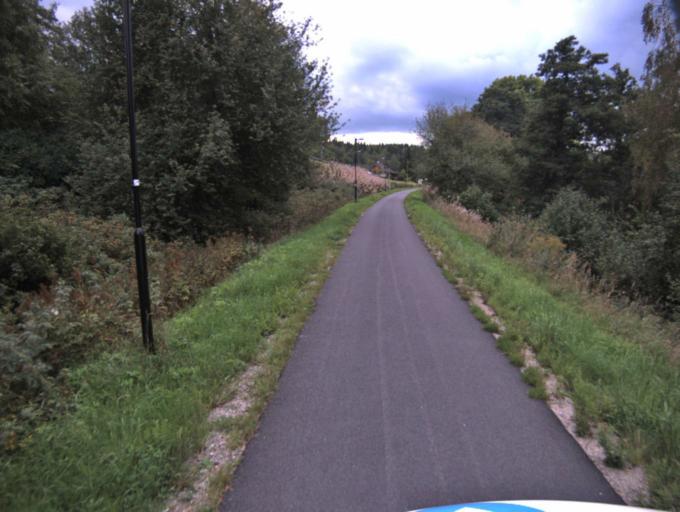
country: SE
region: Vaestra Goetaland
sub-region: Ulricehamns Kommun
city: Ulricehamn
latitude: 57.7727
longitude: 13.4035
